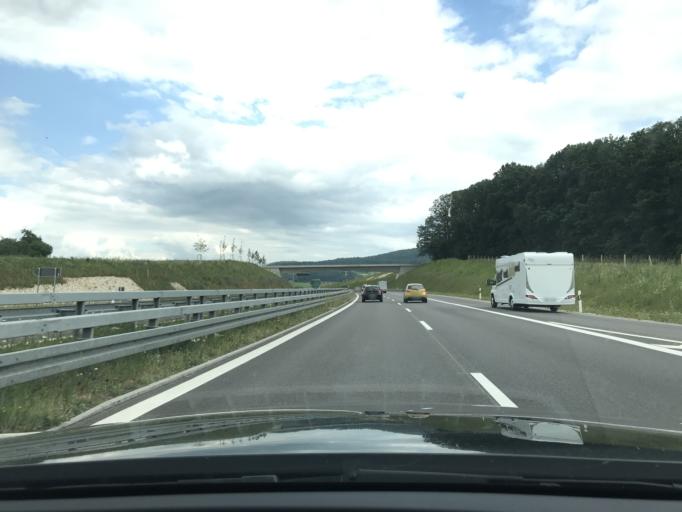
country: DE
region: Baden-Wuerttemberg
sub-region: Regierungsbezirk Stuttgart
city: Mogglingen
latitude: 48.8133
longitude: 9.9559
